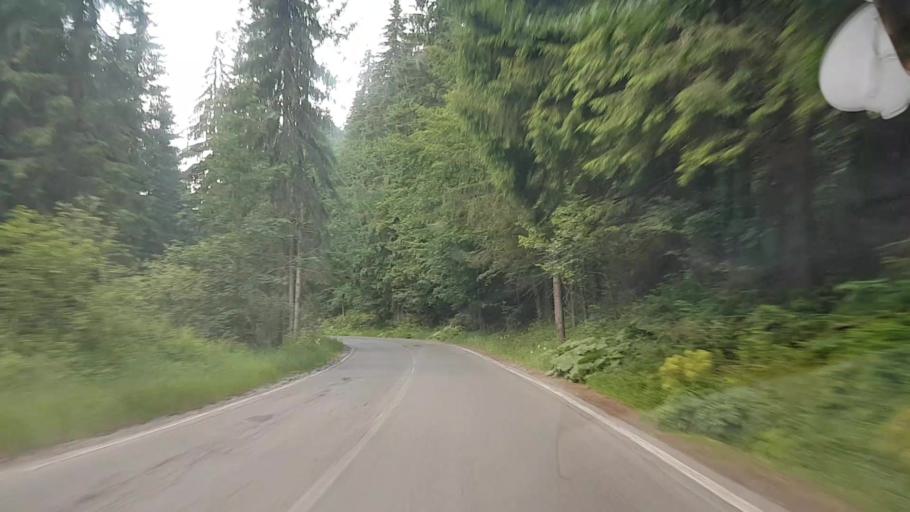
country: RO
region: Harghita
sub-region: Comuna Varsag
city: Varsag
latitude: 46.6301
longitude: 25.2617
